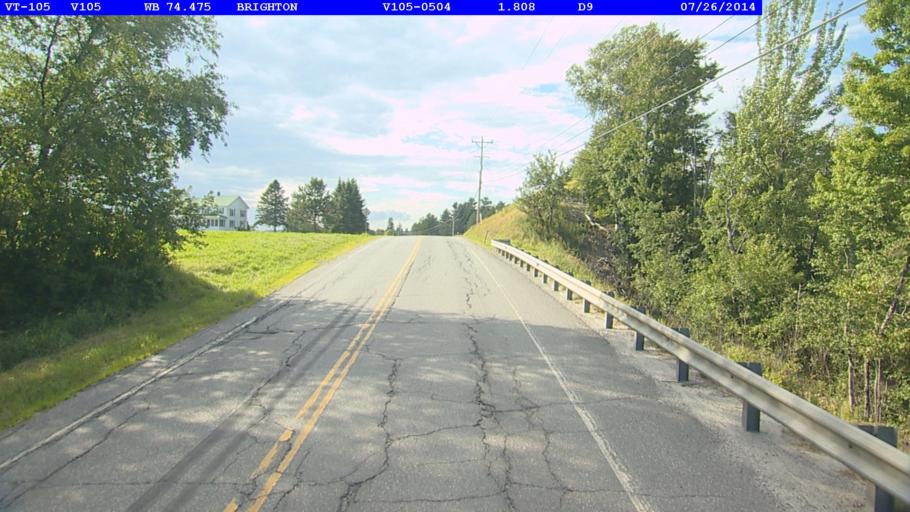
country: US
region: Vermont
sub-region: Caledonia County
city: Lyndonville
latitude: 44.8015
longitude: -71.9156
